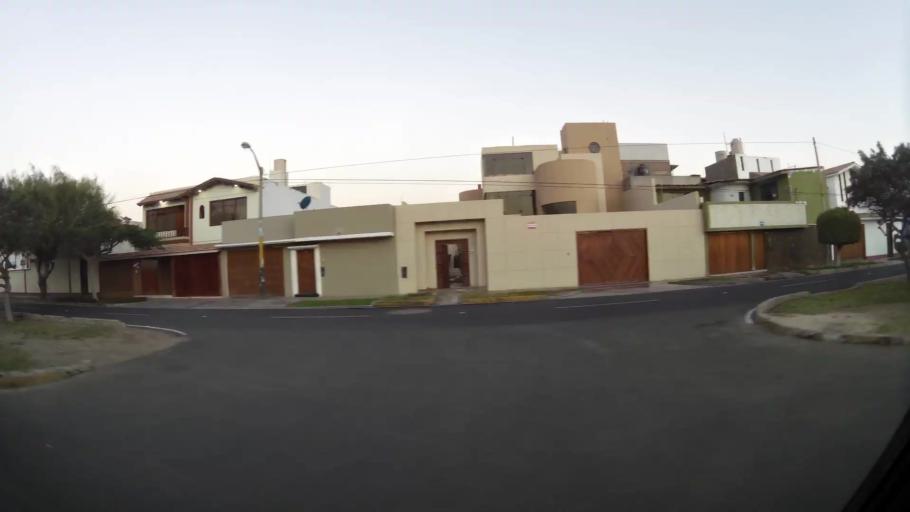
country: PE
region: Ancash
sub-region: Provincia de Santa
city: Buenos Aires
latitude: -9.1250
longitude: -78.5323
